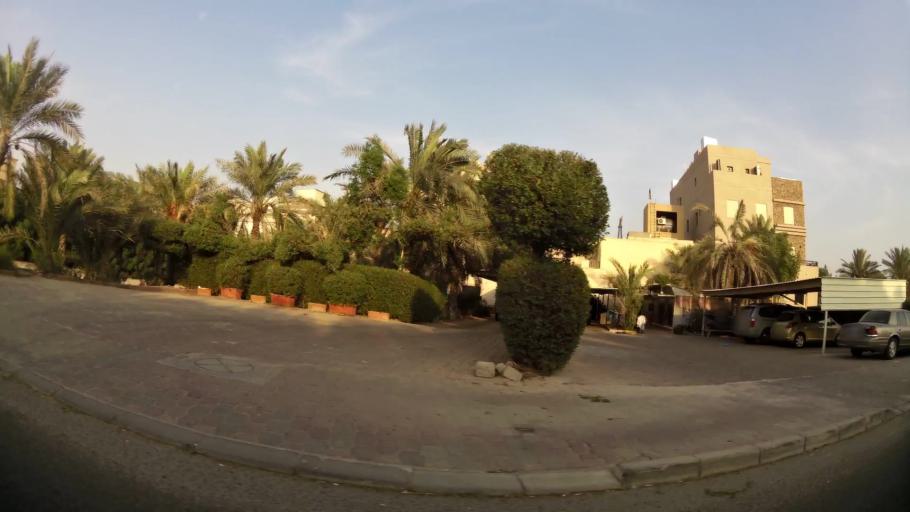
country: KW
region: Mubarak al Kabir
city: Sabah as Salim
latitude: 29.2545
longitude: 48.0709
